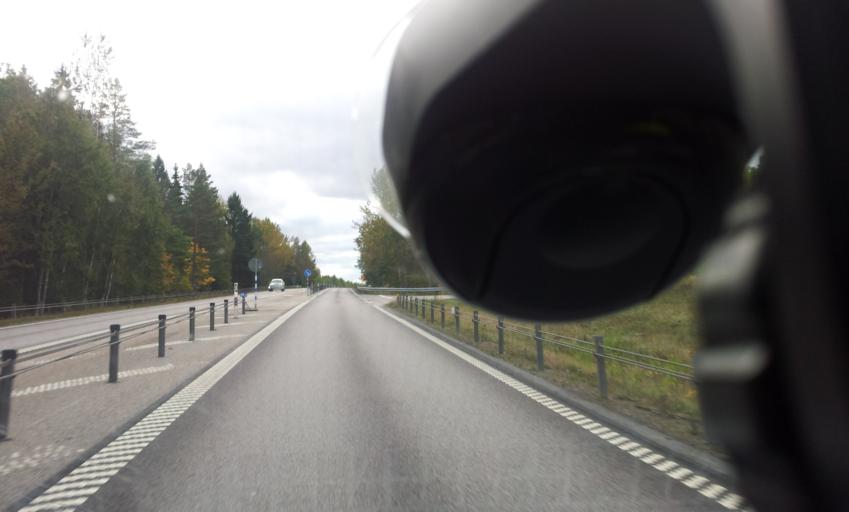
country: SE
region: Kalmar
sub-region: Oskarshamns Kommun
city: Oskarshamn
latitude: 57.2965
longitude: 16.4600
